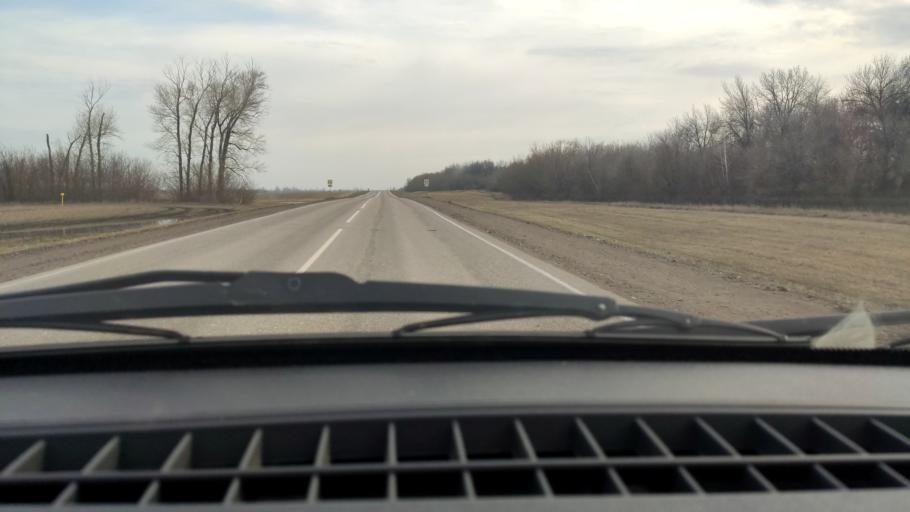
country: RU
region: Bashkortostan
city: Davlekanovo
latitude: 54.2665
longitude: 55.0953
